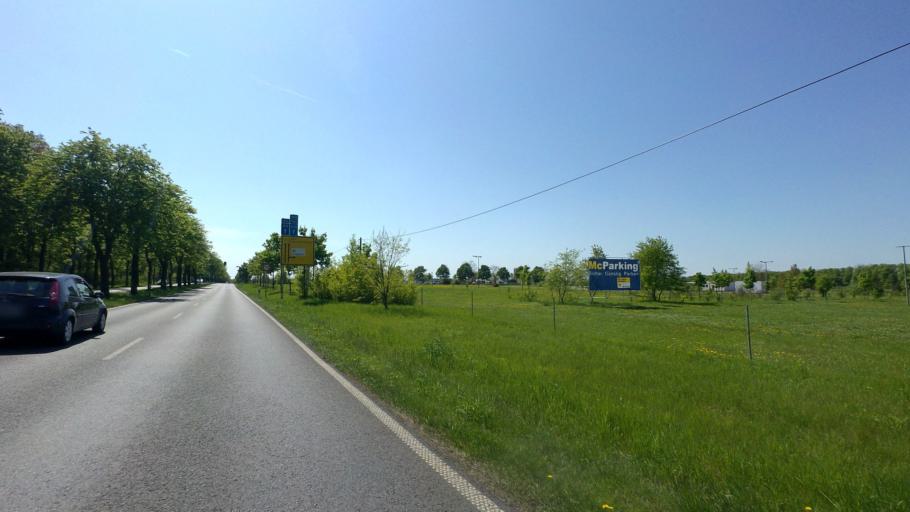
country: DE
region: Brandenburg
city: Wildau
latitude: 52.3106
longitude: 13.6023
